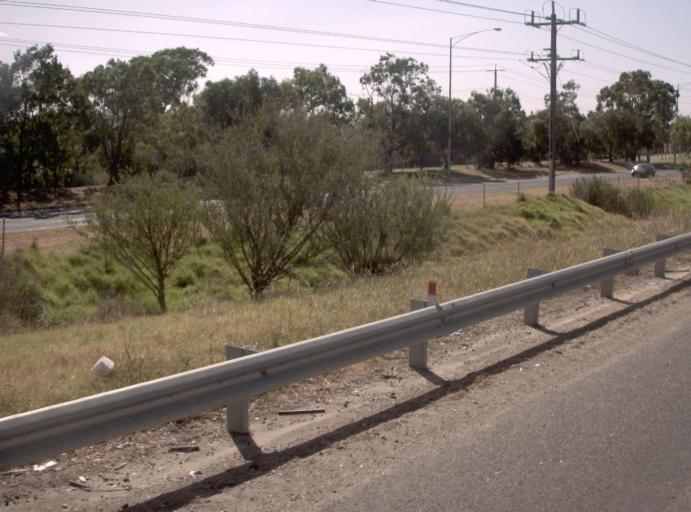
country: AU
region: Victoria
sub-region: Kingston
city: Patterson Lakes
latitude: -38.0574
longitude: 145.1465
